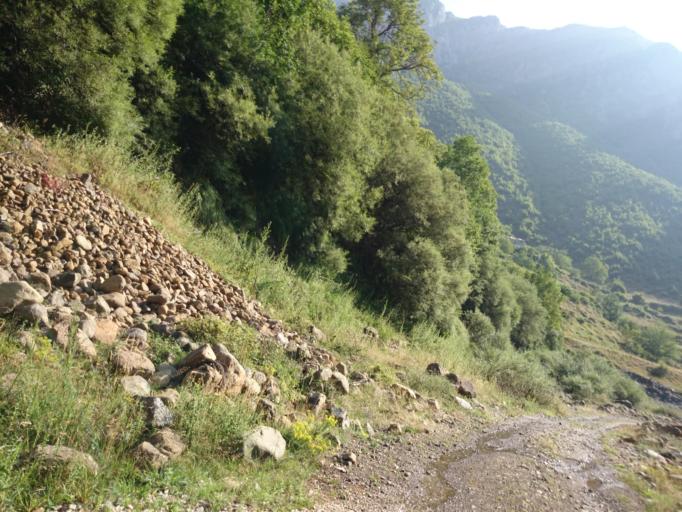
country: AL
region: Diber
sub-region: Rrethi i Dibres
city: Fushe-Lure
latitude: 41.7577
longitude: 20.2298
